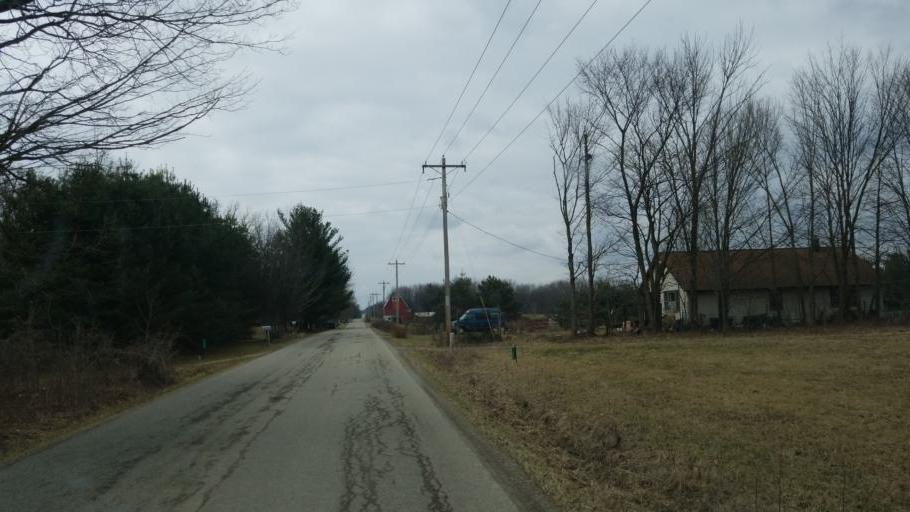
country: US
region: Ohio
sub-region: Knox County
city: Fredericktown
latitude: 40.4325
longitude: -82.6616
